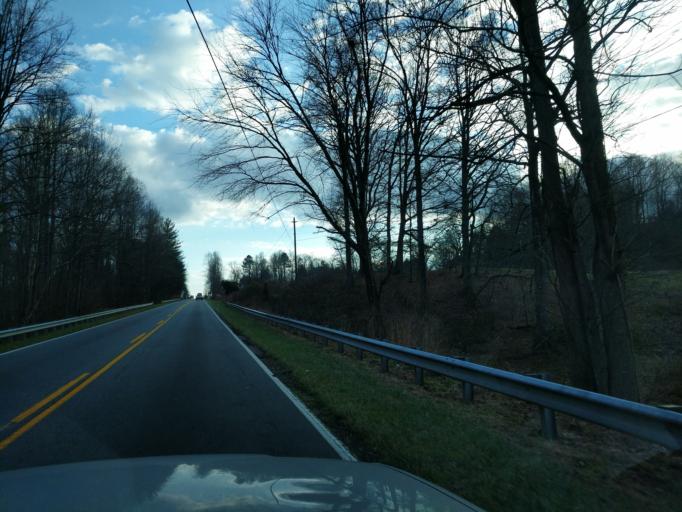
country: US
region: North Carolina
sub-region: McDowell County
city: West Marion
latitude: 35.6212
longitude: -81.9862
